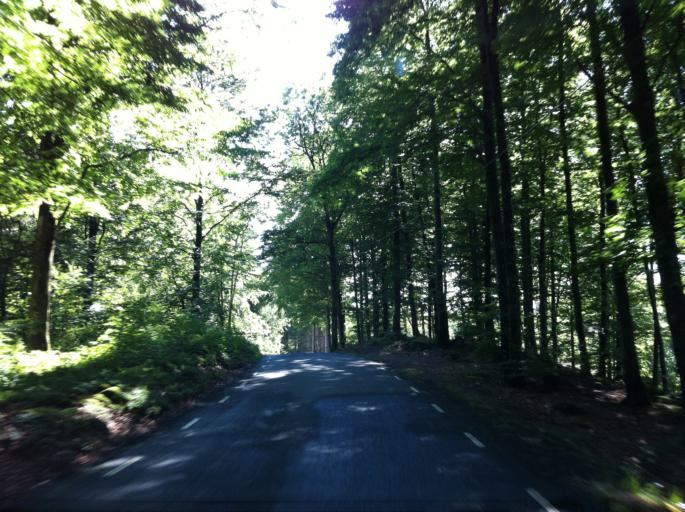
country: SE
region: Skane
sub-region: Hassleholms Kommun
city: Sosdala
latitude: 56.0449
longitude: 13.6133
